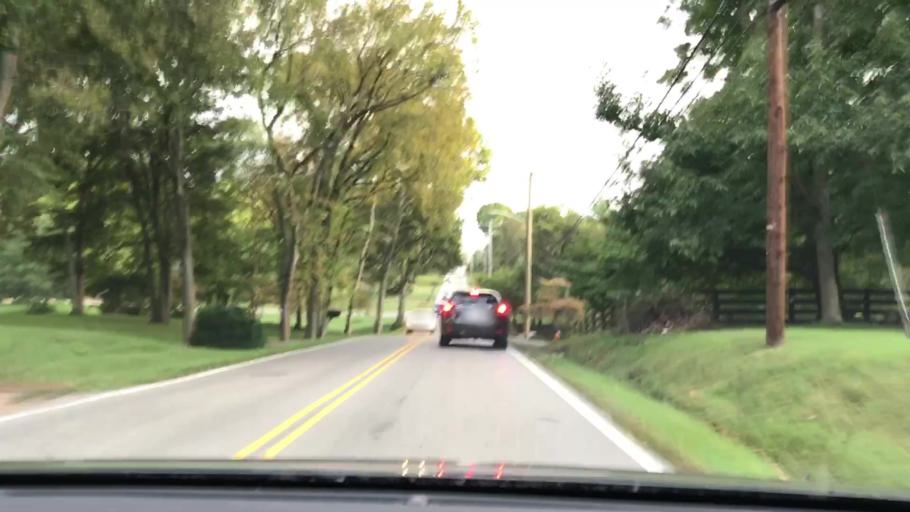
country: US
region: Tennessee
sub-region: Williamson County
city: Brentwood Estates
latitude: 36.0342
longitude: -86.7688
